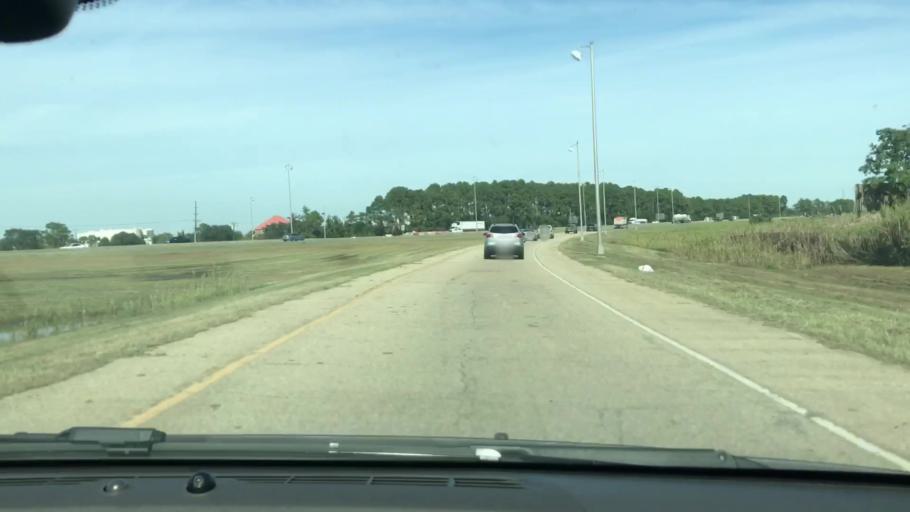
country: US
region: Louisiana
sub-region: Saint Tammany Parish
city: Eden Isle
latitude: 30.2233
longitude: -89.7802
